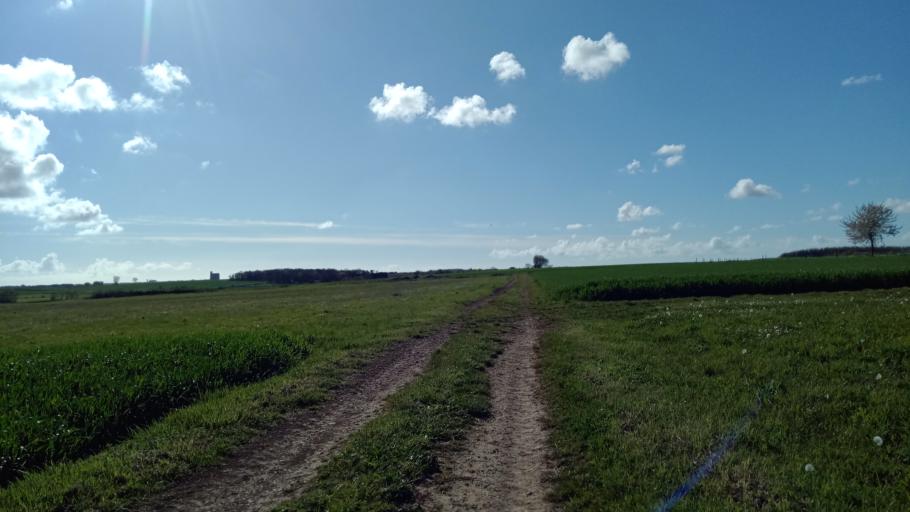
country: FR
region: Poitou-Charentes
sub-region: Departement de la Charente-Maritime
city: Verines
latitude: 46.1571
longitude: -0.9378
